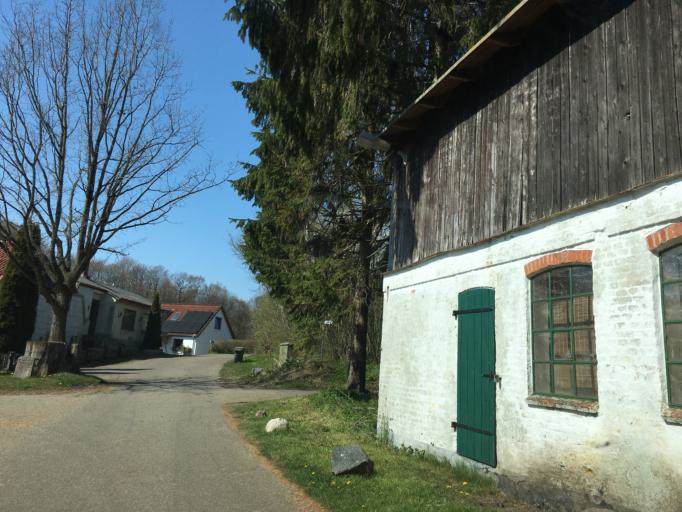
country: DE
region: Schleswig-Holstein
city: Nottfeld
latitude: 54.5944
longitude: 9.8003
